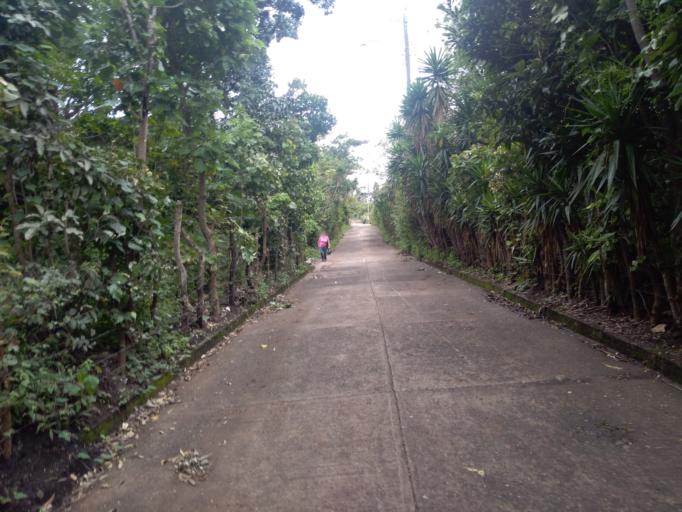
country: GT
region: Escuintla
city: San Vicente Pacaya
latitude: 14.3703
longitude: -90.5665
